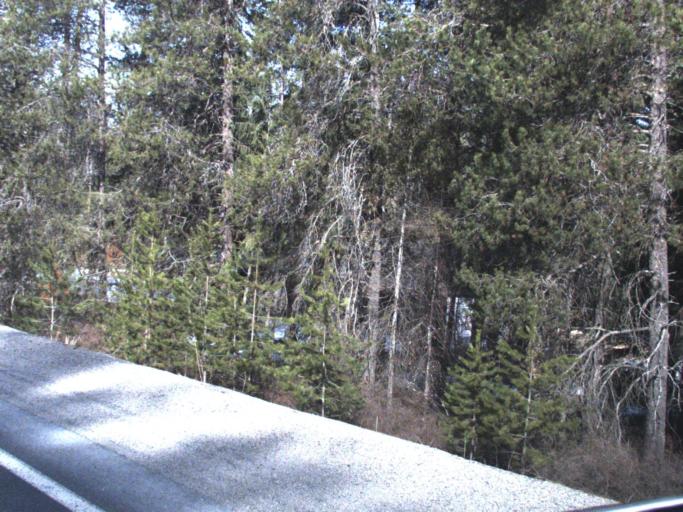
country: US
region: Washington
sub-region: Stevens County
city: Colville
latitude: 48.5204
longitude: -117.6908
